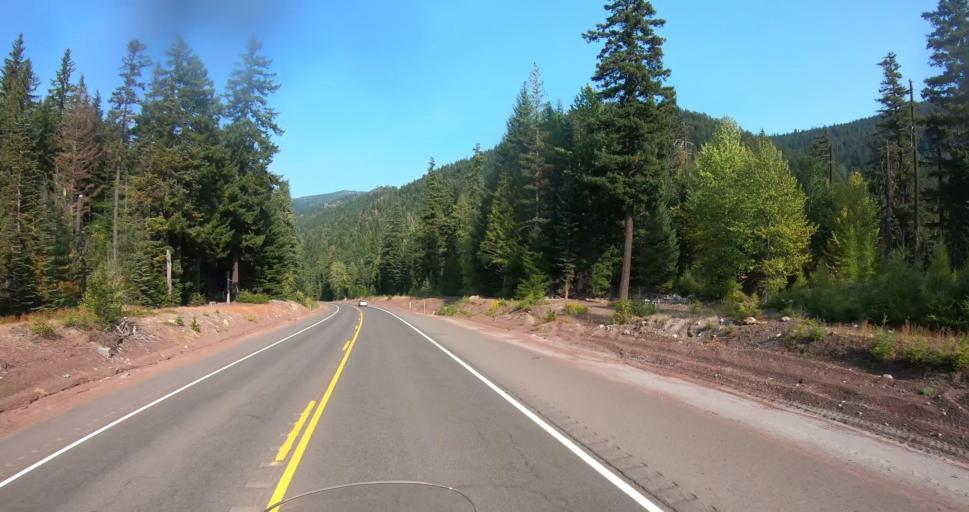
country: US
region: Oregon
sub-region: Hood River County
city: Odell
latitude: 45.3347
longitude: -121.5759
